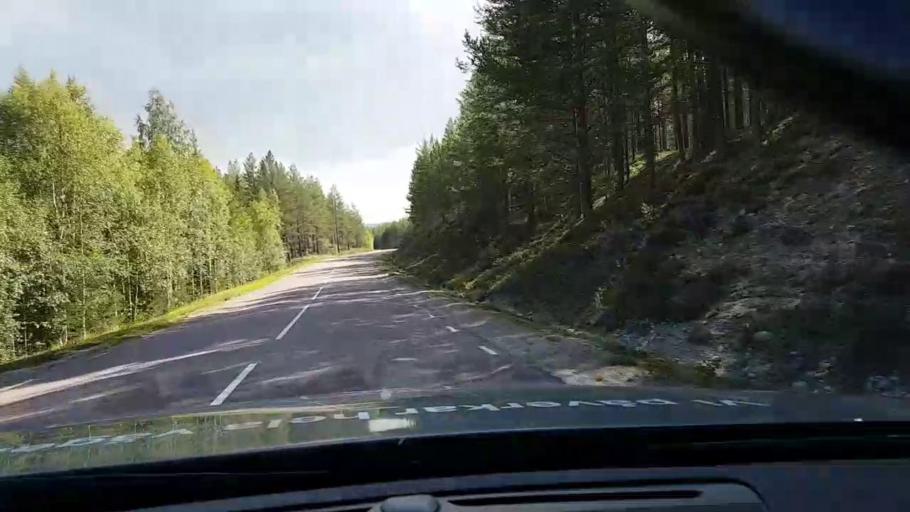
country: SE
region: Vaesterbotten
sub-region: Asele Kommun
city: Asele
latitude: 63.8831
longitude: 17.3536
